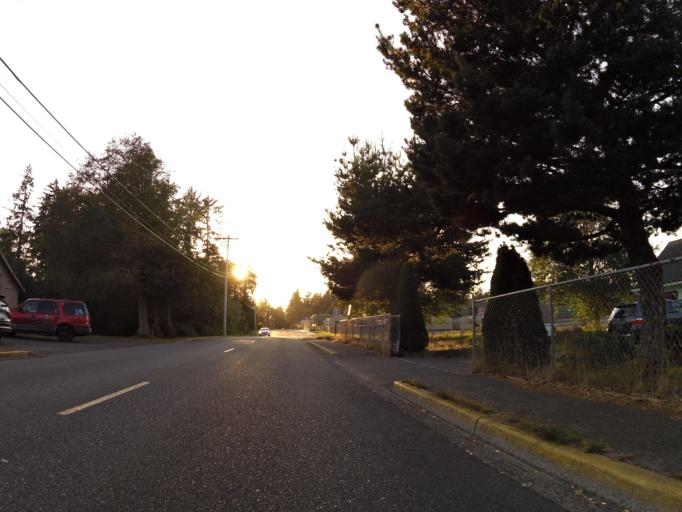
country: US
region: Oregon
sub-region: Clatsop County
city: Warrenton
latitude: 46.1577
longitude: -123.9290
